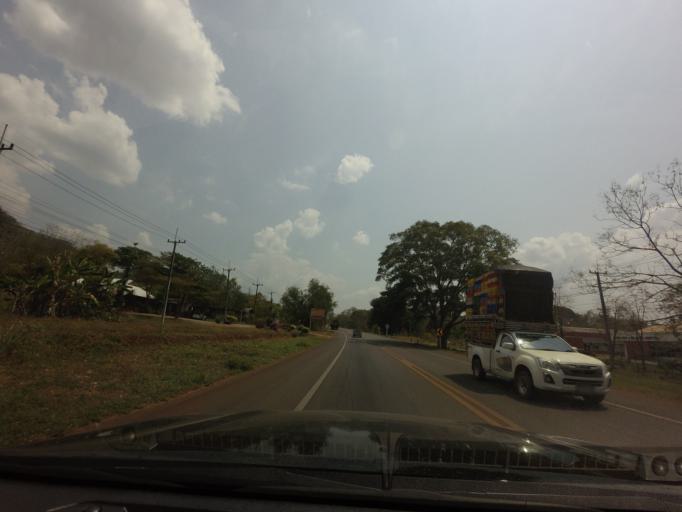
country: TH
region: Kanchanaburi
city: Sai Yok
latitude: 14.1373
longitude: 99.1507
